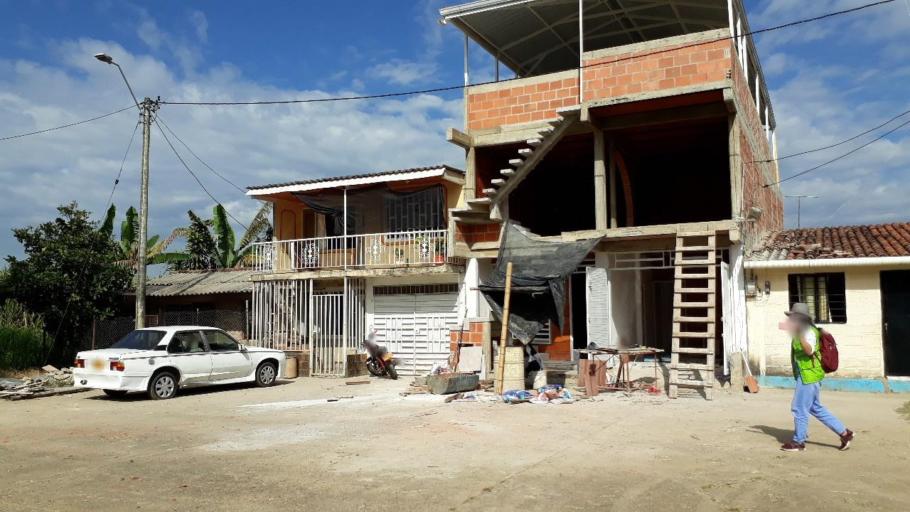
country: CO
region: Valle del Cauca
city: Jamundi
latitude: 3.1719
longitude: -76.5939
